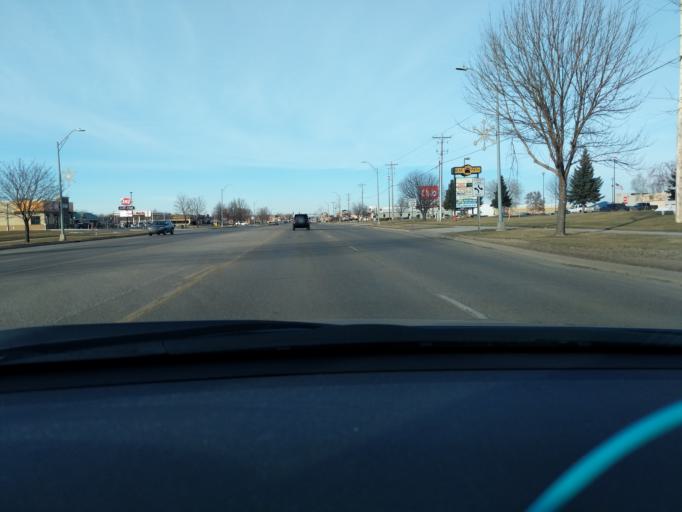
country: US
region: Minnesota
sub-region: Kandiyohi County
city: Willmar
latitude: 45.1000
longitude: -95.0426
